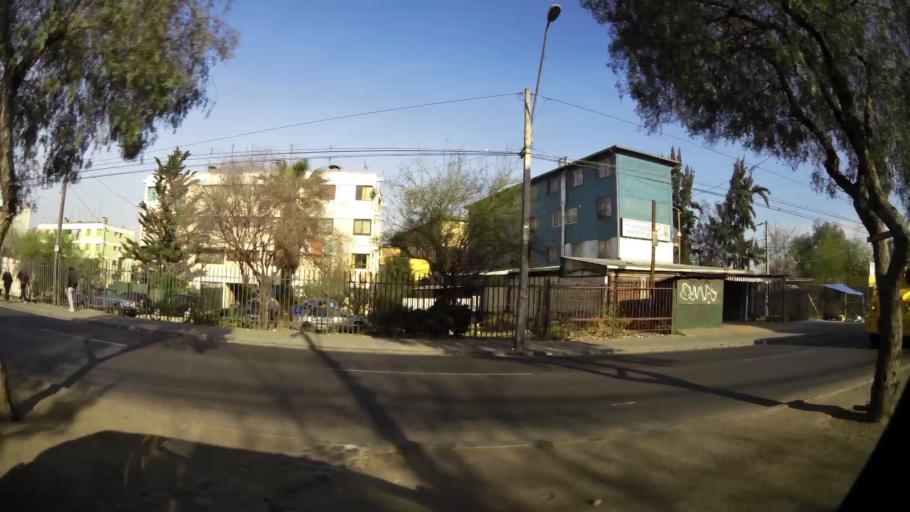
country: CL
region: Santiago Metropolitan
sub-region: Provincia de Santiago
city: Lo Prado
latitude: -33.4429
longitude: -70.7406
